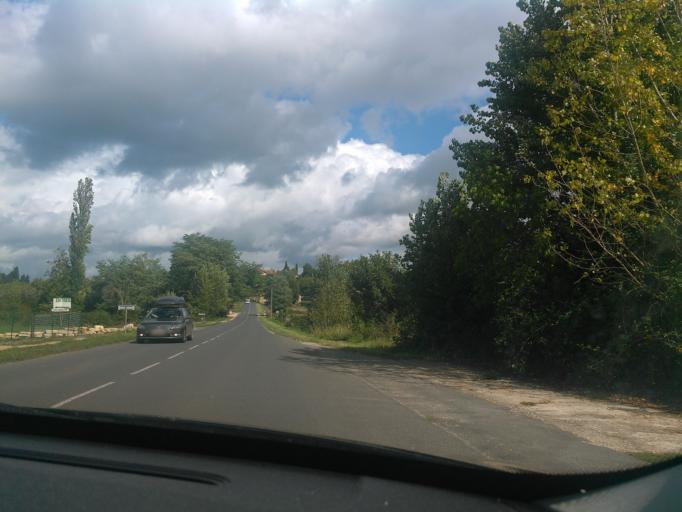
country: FR
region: Aquitaine
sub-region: Departement de la Dordogne
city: Cenac-et-Saint-Julien
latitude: 44.8193
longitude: 1.1555
